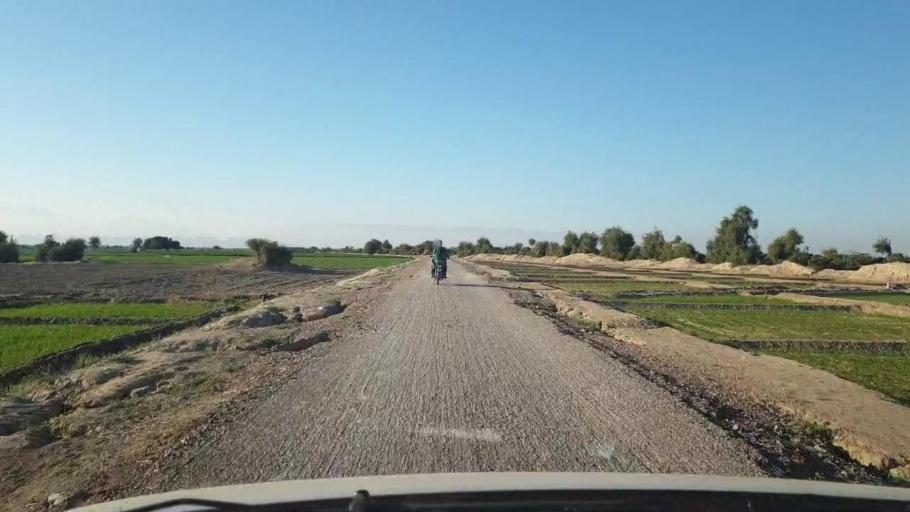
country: PK
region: Sindh
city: Johi
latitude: 26.7641
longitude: 67.4650
